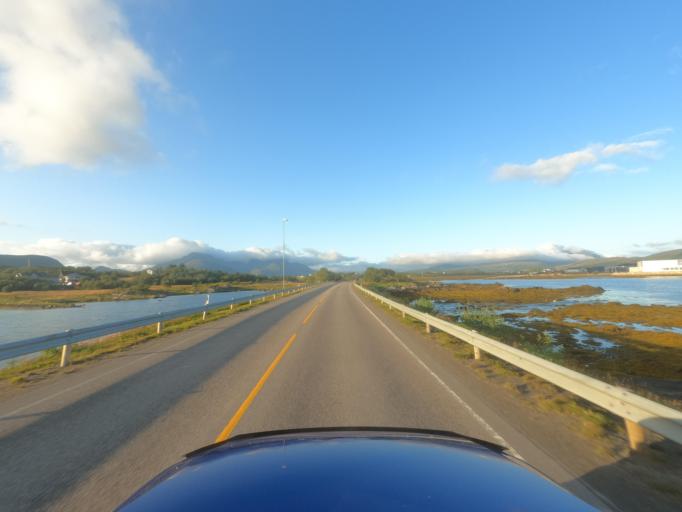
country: NO
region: Nordland
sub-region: Vestvagoy
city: Gravdal
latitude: 68.1282
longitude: 13.5516
